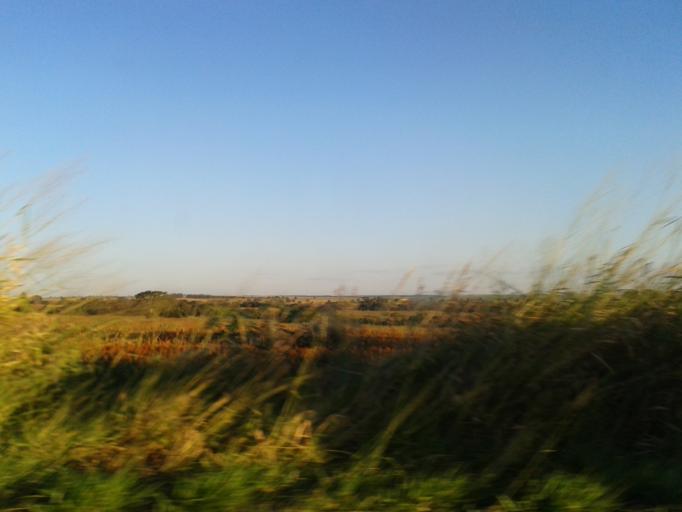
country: BR
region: Minas Gerais
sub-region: Centralina
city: Centralina
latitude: -18.7328
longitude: -49.2429
